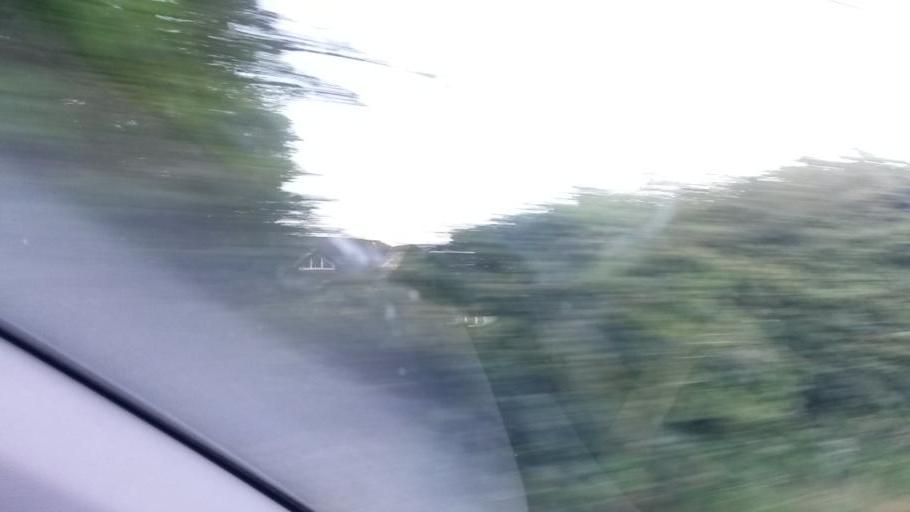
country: IE
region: Leinster
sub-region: An Mhi
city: Ashbourne
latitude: 53.5785
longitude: -6.3785
